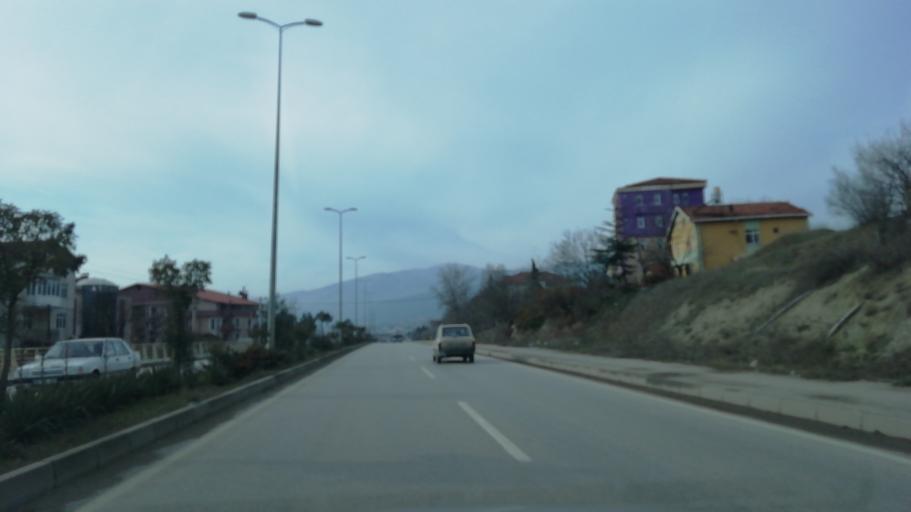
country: TR
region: Karabuk
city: Safranbolu
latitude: 41.2182
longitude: 32.6843
